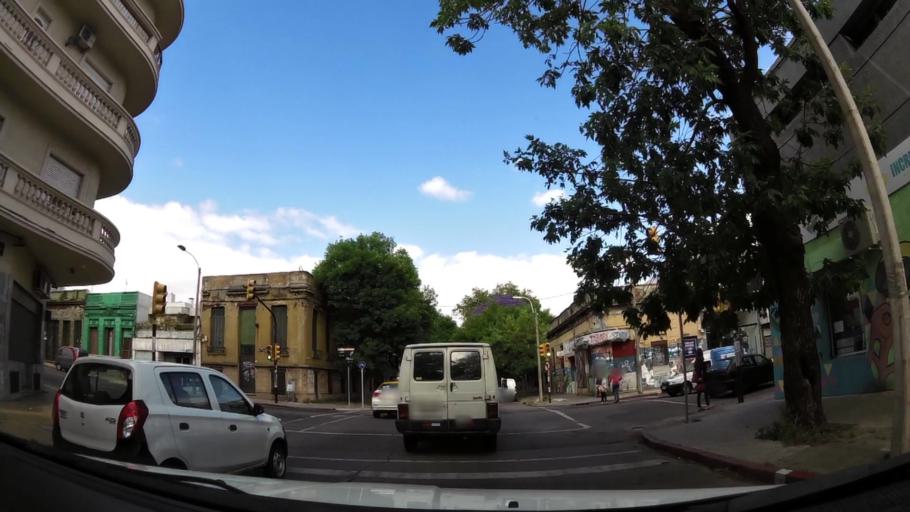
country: UY
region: Montevideo
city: Montevideo
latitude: -34.8891
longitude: -56.1789
